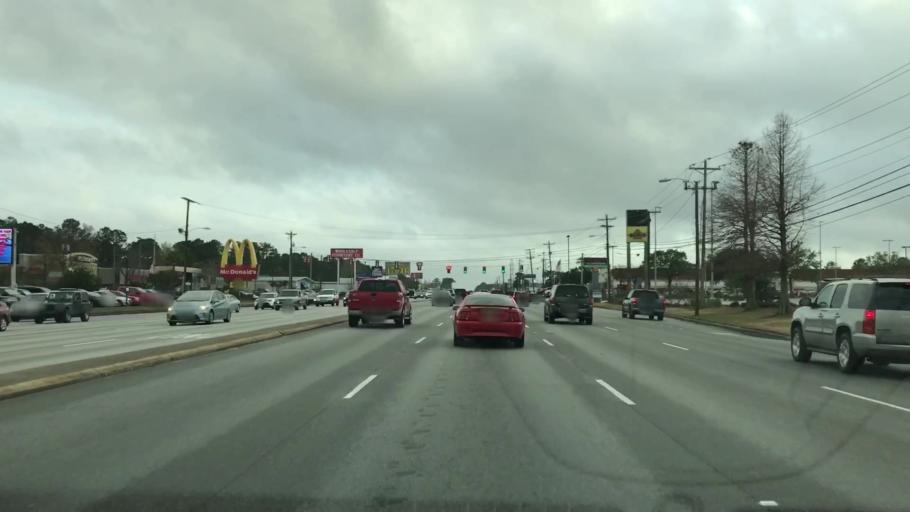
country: US
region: South Carolina
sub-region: Berkeley County
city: Goose Creek
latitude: 32.9644
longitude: -80.0442
